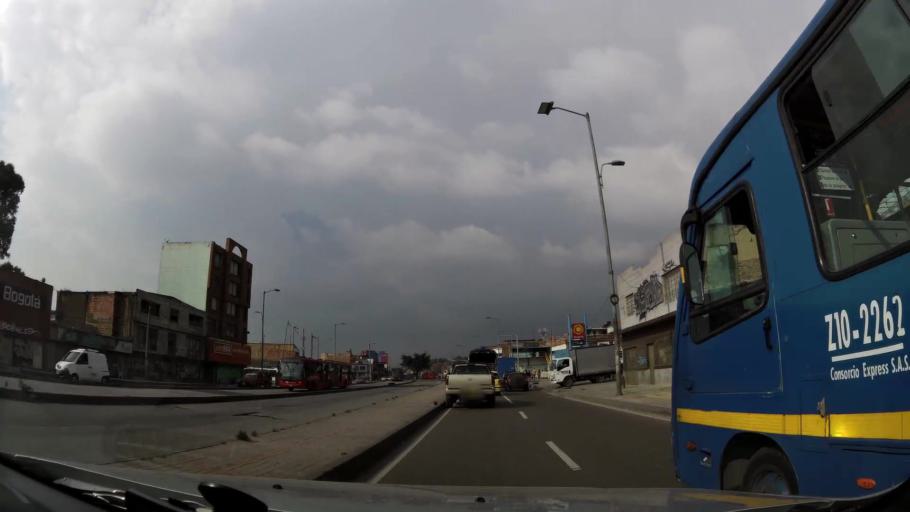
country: CO
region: Bogota D.C.
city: Bogota
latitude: 4.5678
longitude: -74.1262
